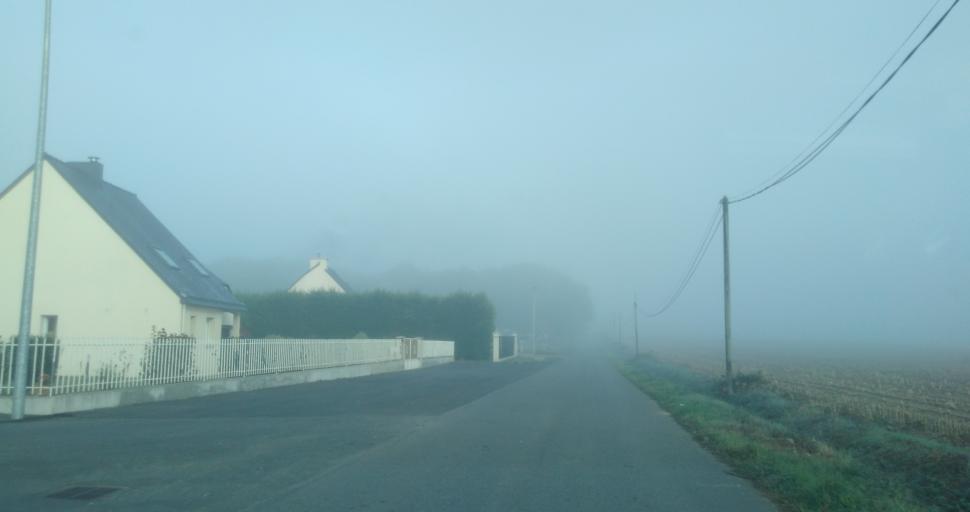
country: FR
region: Brittany
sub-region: Departement d'Ille-et-Vilaine
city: Boisgervilly
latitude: 48.1113
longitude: -2.1260
